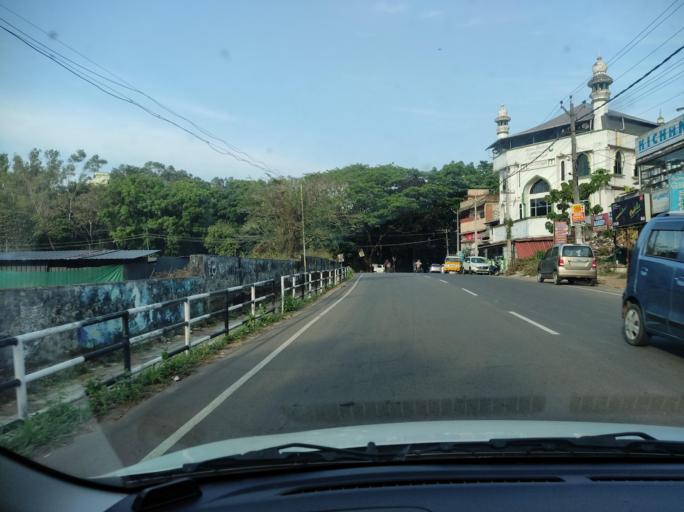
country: IN
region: Kerala
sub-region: Kottayam
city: Kottayam
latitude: 9.6358
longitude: 76.5271
